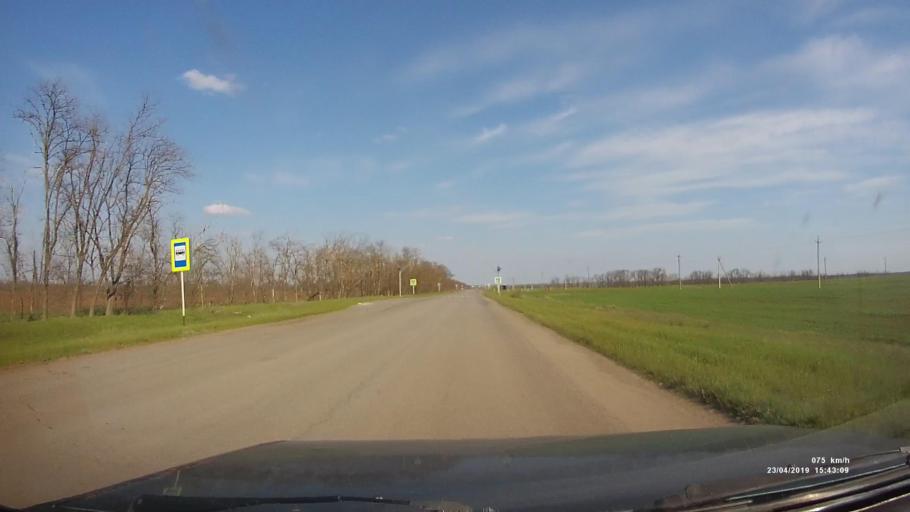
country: RU
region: Rostov
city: Remontnoye
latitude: 46.5458
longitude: 43.0782
